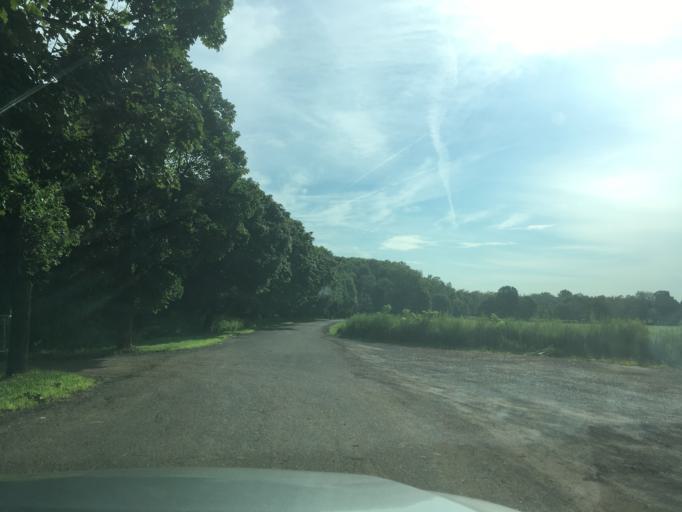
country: US
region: New Jersey
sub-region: Mercer County
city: Princeton
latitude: 40.3402
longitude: -74.6428
